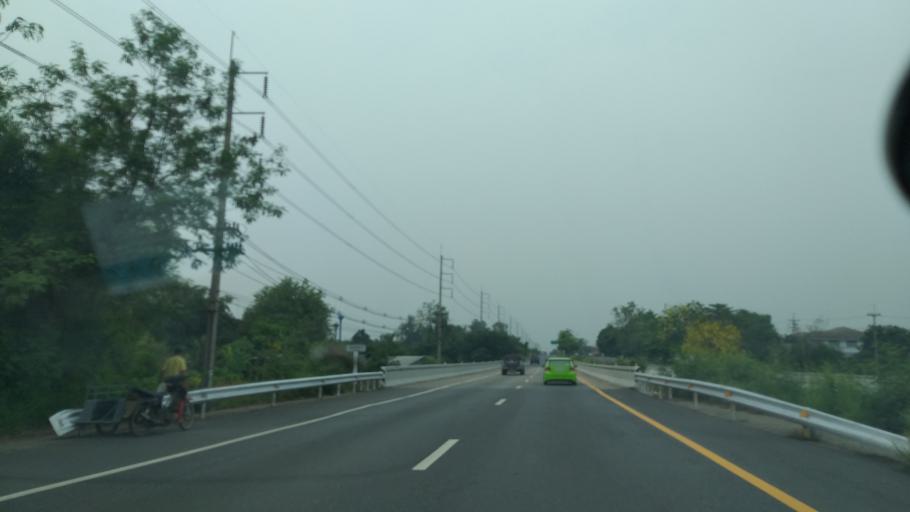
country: TH
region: Chon Buri
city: Ko Chan
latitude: 13.4106
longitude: 101.2821
